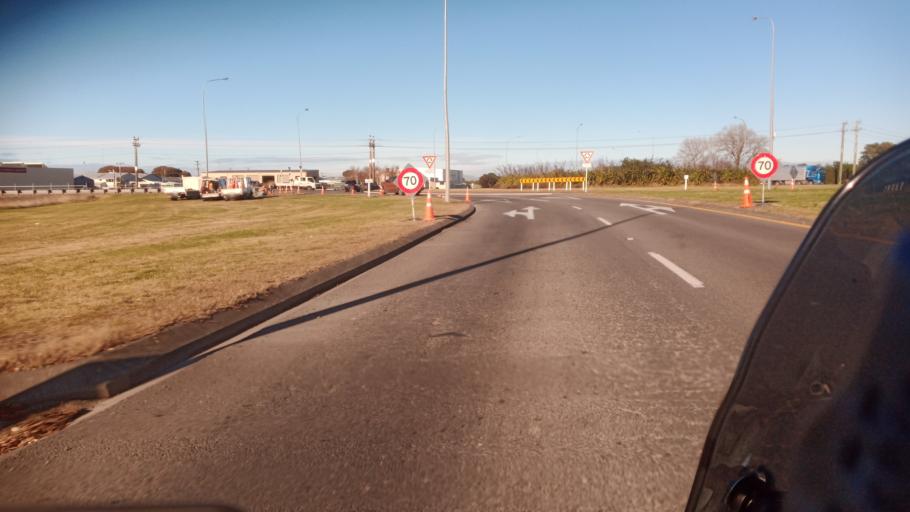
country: NZ
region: Hawke's Bay
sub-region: Napier City
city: Napier
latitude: -39.4956
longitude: 176.8743
